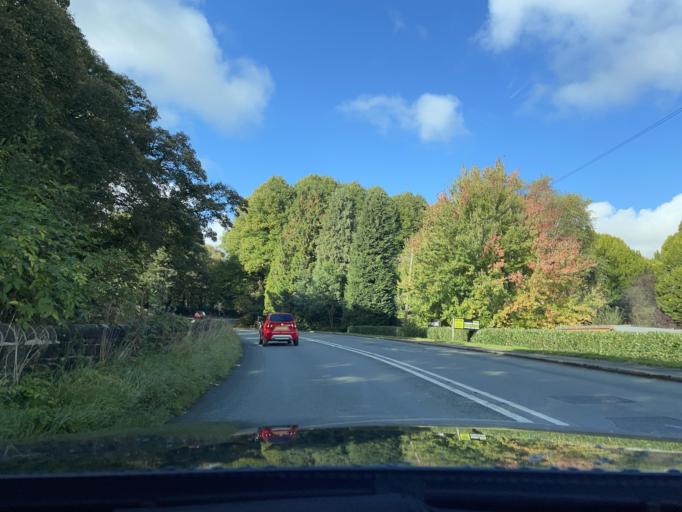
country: GB
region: England
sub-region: Derbyshire
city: Hathersage
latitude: 53.3400
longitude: -1.6951
